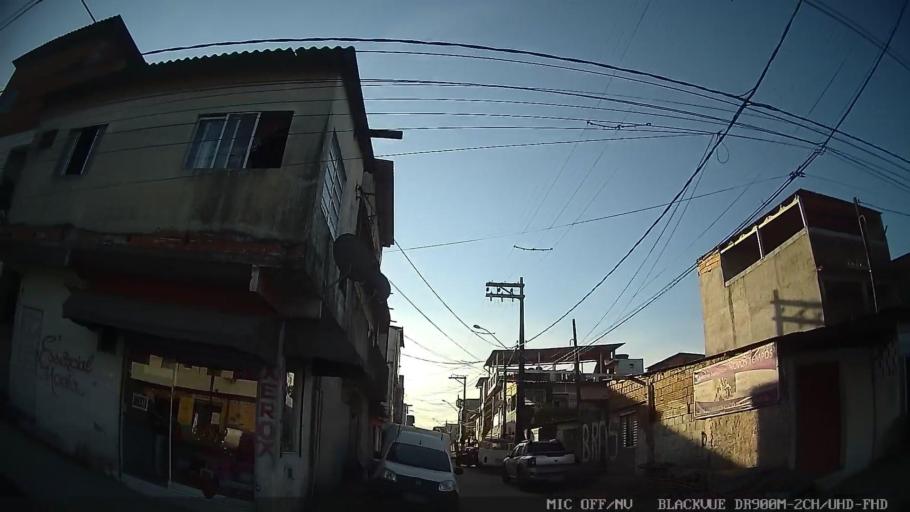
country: BR
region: Sao Paulo
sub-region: Guaruja
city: Guaruja
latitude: -23.9628
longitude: -46.2456
